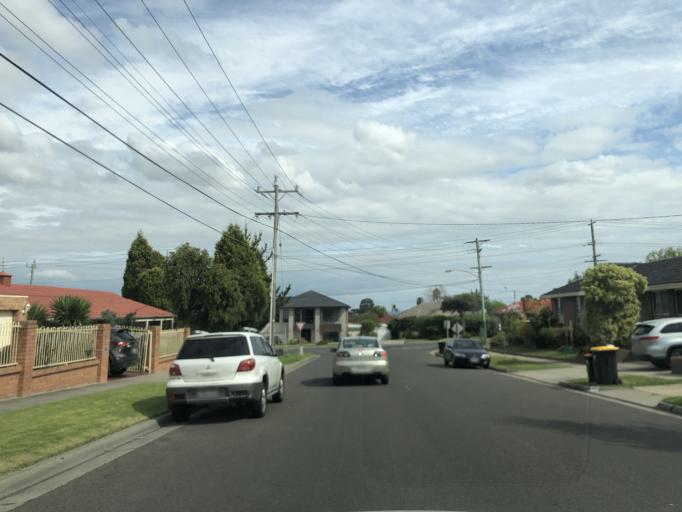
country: AU
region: Victoria
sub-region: Greater Dandenong
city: Noble Park North
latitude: -37.9549
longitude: 145.1988
